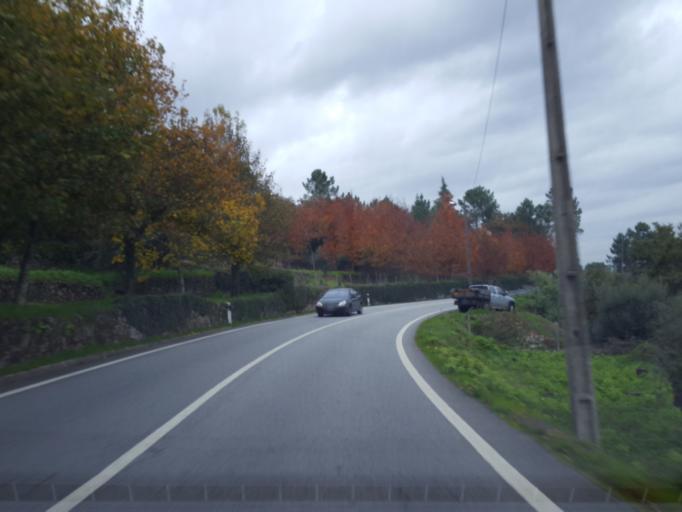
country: PT
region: Porto
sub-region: Marco de Canaveses
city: Marco de Canavezes
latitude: 41.1642
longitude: -8.1455
